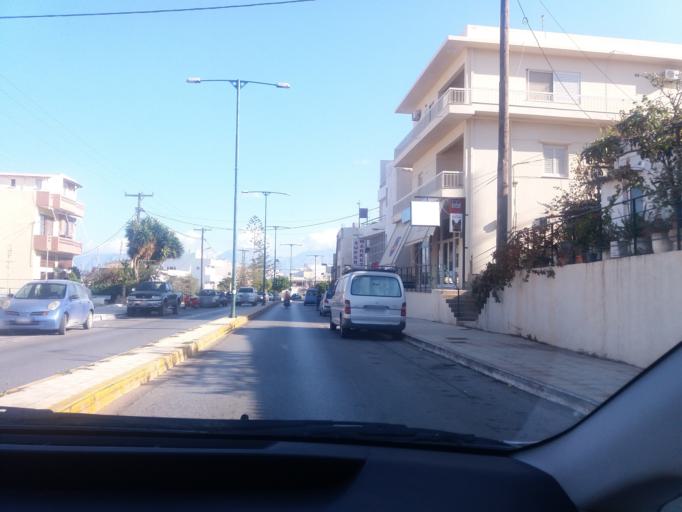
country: GR
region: Crete
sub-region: Nomos Lasithiou
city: Agios Nikolaos
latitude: 35.1964
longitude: 25.7116
